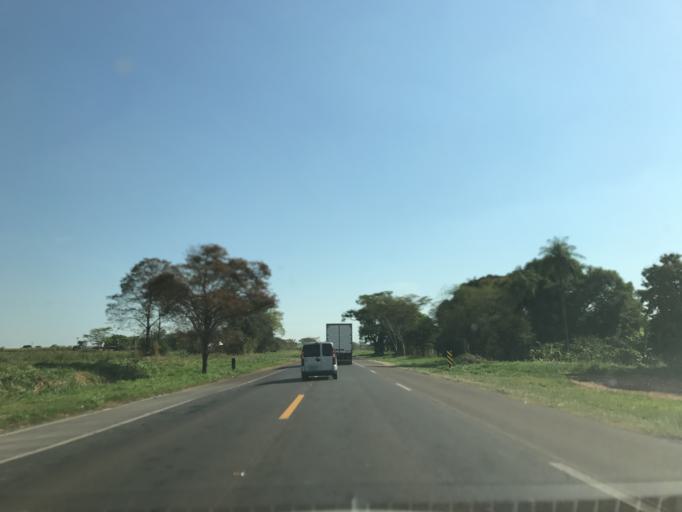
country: BR
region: Sao Paulo
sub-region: Penapolis
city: Penapolis
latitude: -21.4785
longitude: -50.2001
